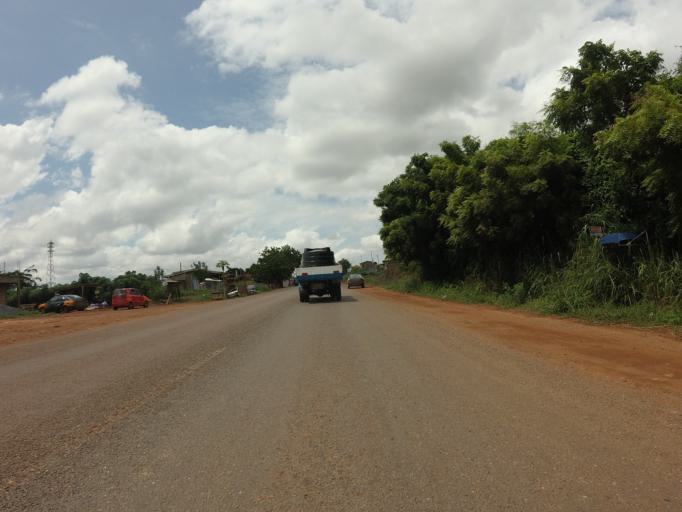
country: GH
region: Eastern
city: Aburi
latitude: 5.8187
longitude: -0.1209
